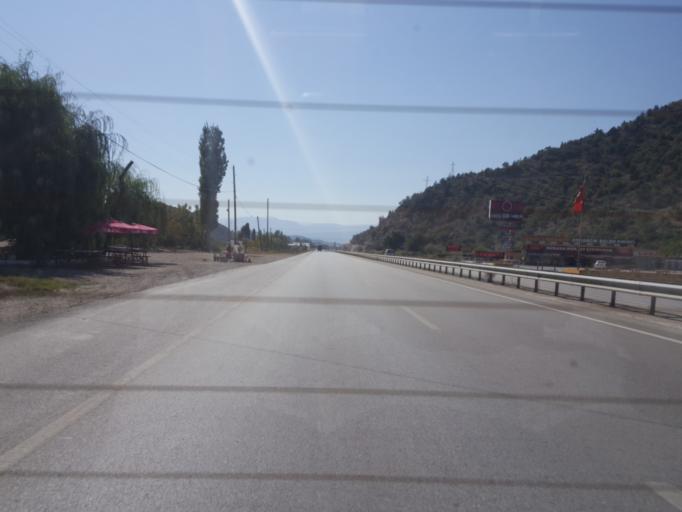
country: TR
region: Corum
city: Osmancik
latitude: 40.9735
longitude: 34.9121
